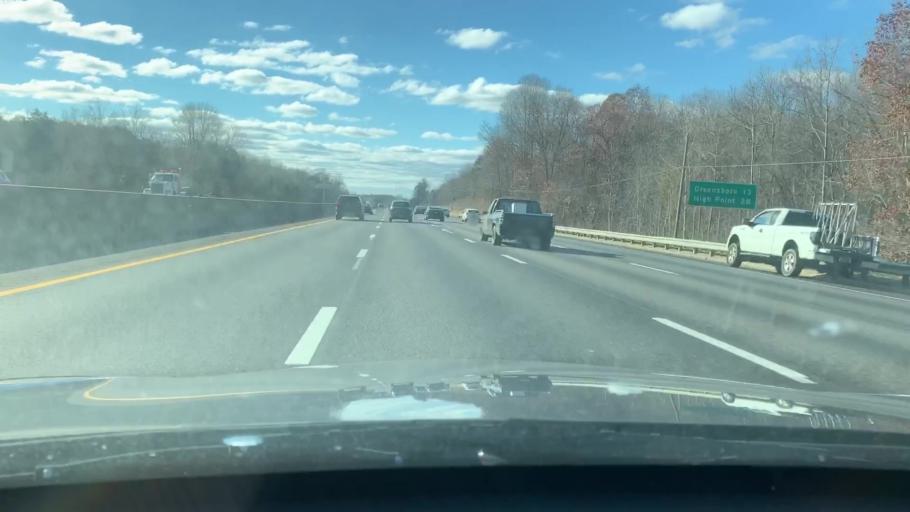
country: US
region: North Carolina
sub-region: Guilford County
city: Gibsonville
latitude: 36.0621
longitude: -79.5812
